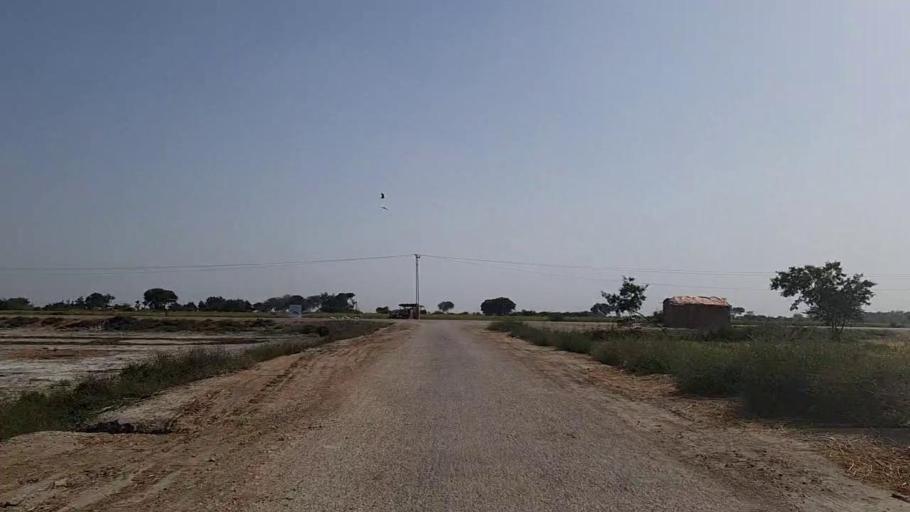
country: PK
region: Sindh
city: Jati
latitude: 24.3510
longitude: 68.2760
